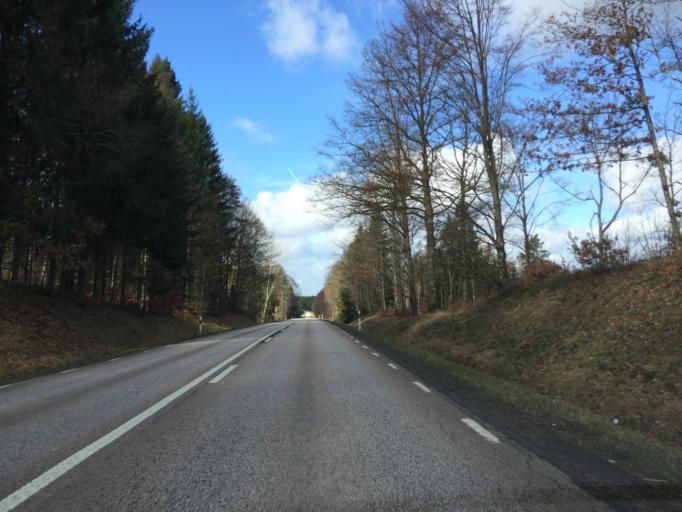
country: SE
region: Kronoberg
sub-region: Markaryds Kommun
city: Markaryd
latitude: 56.4782
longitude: 13.4880
